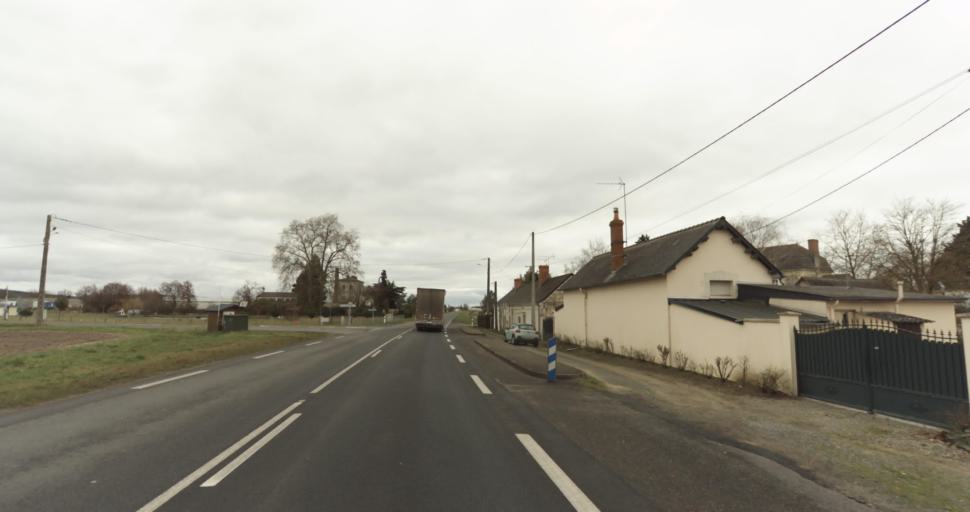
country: FR
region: Pays de la Loire
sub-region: Departement de Maine-et-Loire
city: Allonnes
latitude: 47.3021
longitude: -0.0123
